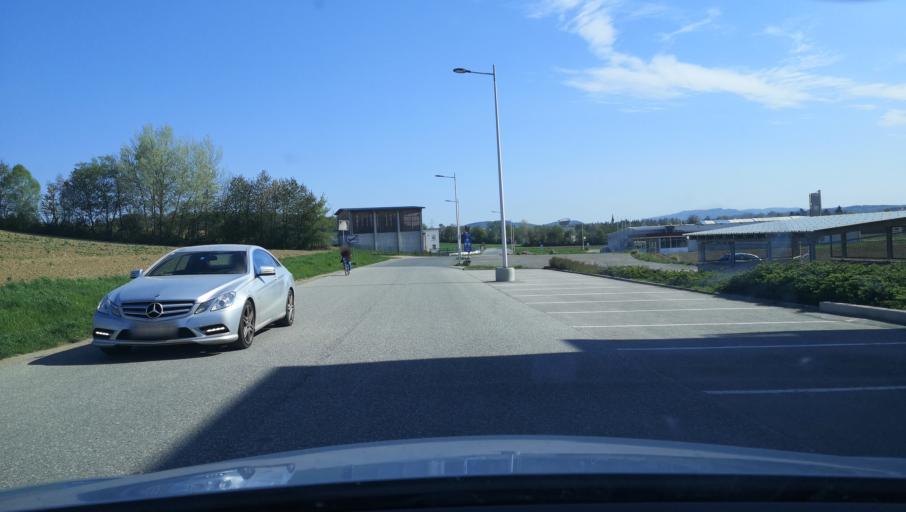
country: AT
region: Lower Austria
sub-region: Politischer Bezirk Scheibbs
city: Wieselburg
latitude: 48.1394
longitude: 15.1390
